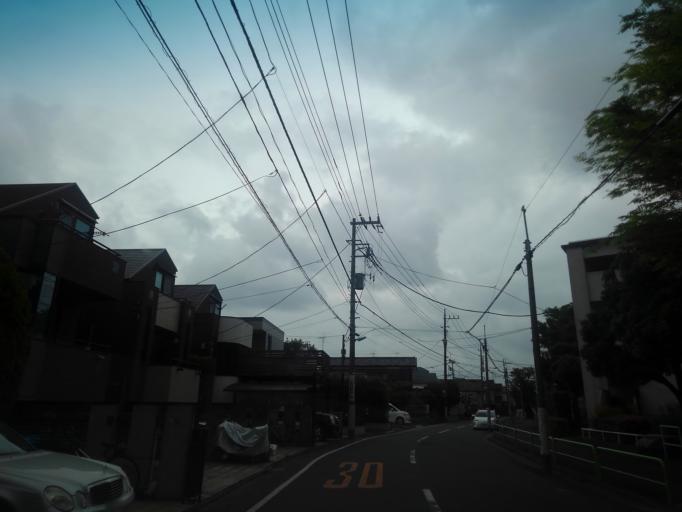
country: JP
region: Tokyo
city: Musashino
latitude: 35.7147
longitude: 139.5863
